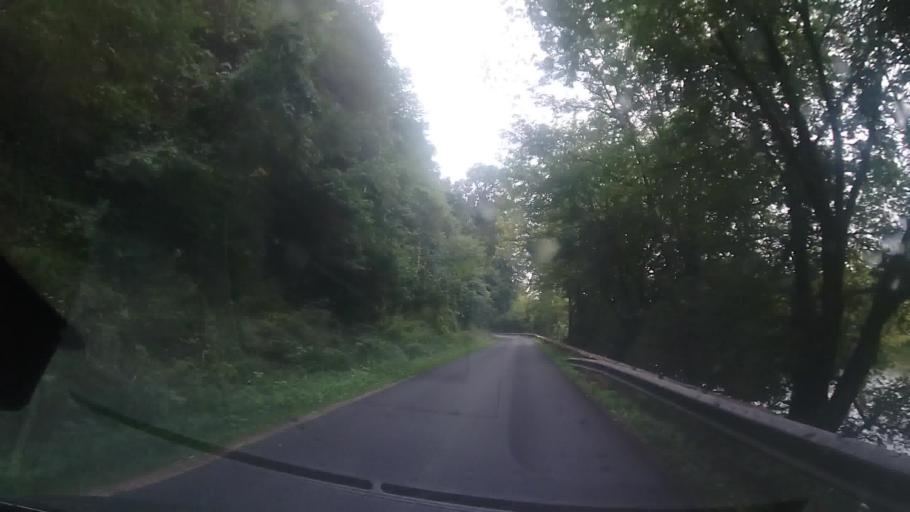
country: FR
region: Aquitaine
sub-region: Departement de la Dordogne
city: Domme
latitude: 44.8058
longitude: 1.2151
